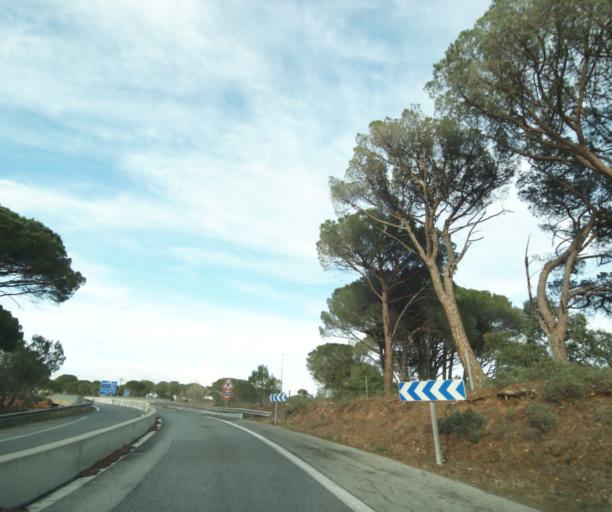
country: FR
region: Provence-Alpes-Cote d'Azur
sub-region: Departement du Var
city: Le Muy
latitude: 43.4582
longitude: 6.5536
